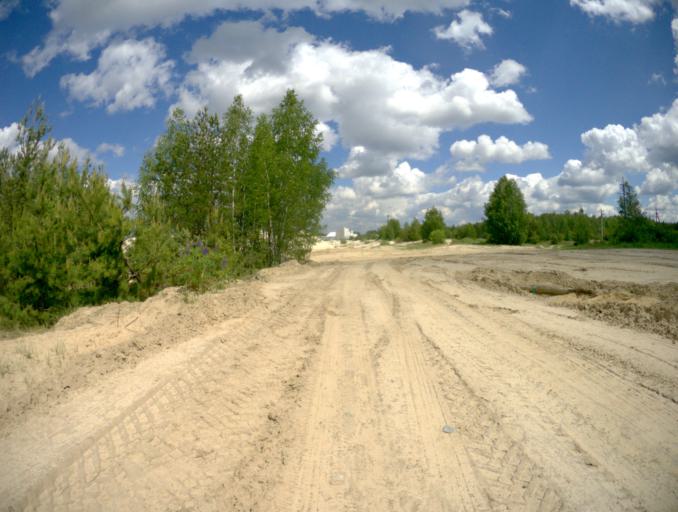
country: RU
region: Vladimir
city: Velikodvorskiy
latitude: 55.2292
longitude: 40.6462
